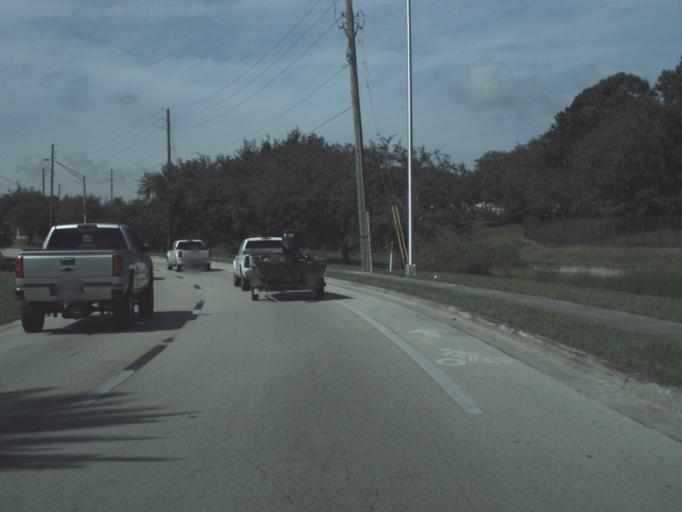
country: US
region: Florida
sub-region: Polk County
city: Cypress Gardens
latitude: 28.0053
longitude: -81.7070
